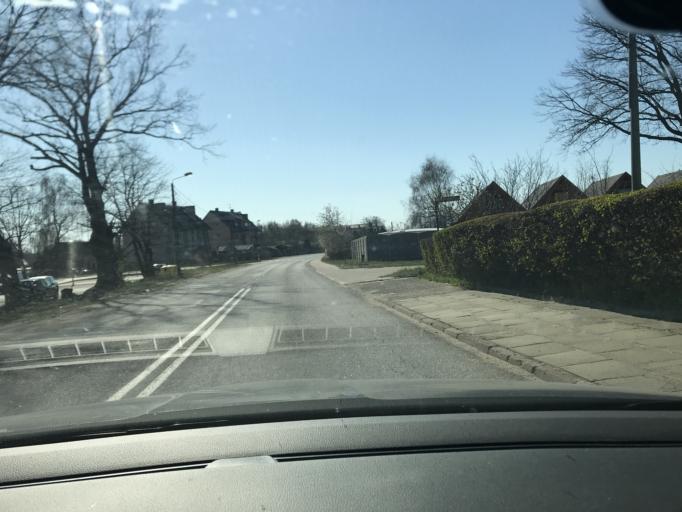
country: PL
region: Pomeranian Voivodeship
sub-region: Powiat nowodworski
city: Sztutowo
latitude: 54.3330
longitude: 19.1868
